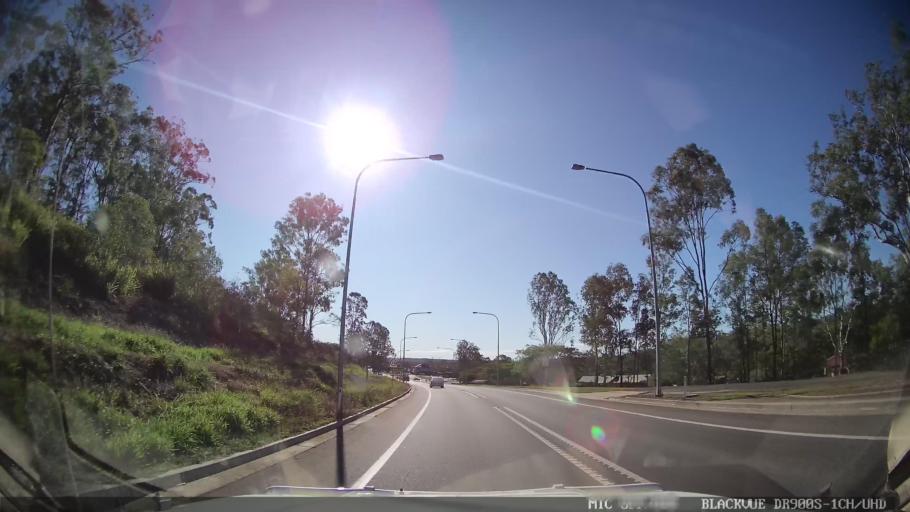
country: AU
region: Queensland
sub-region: Bundaberg
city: Sharon
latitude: -24.9955
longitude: 151.9603
